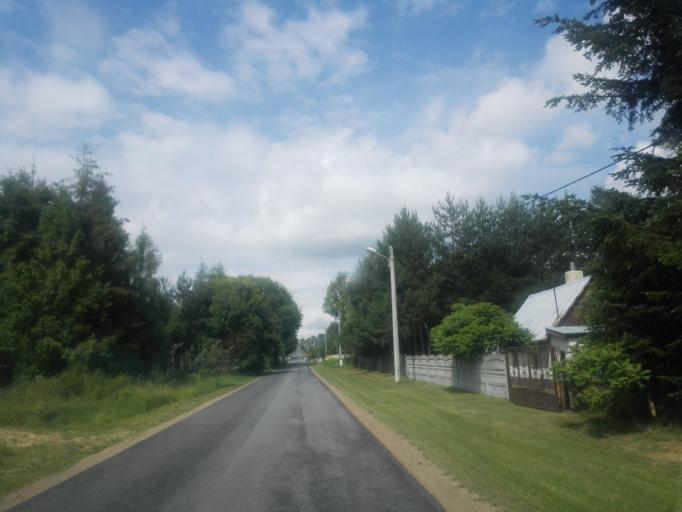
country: PL
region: Silesian Voivodeship
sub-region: Powiat myszkowski
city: Choron
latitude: 50.7064
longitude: 19.3032
